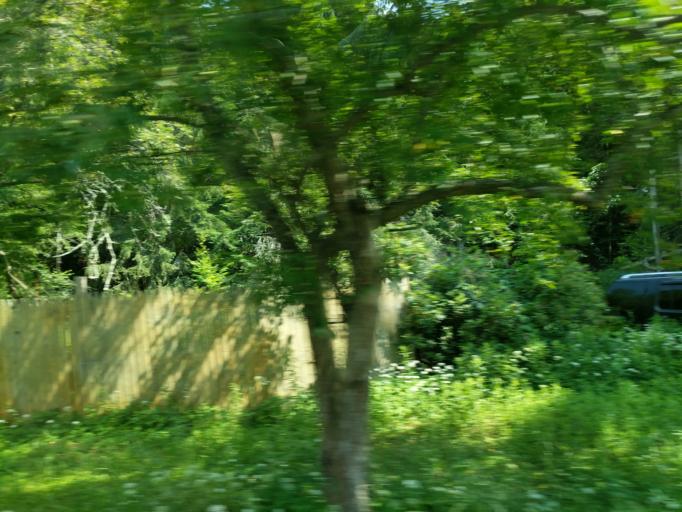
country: US
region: New York
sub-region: Sullivan County
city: Livingston Manor
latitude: 41.9246
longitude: -74.9273
